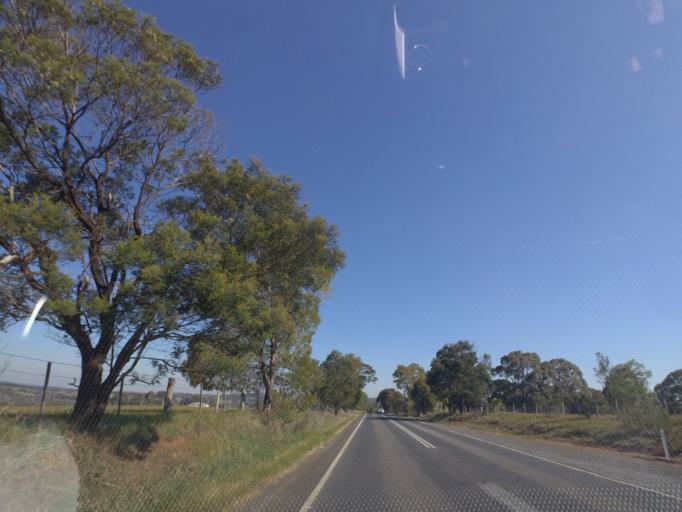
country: AU
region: Victoria
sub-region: Whittlesea
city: Whittlesea
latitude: -37.3322
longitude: 144.9834
